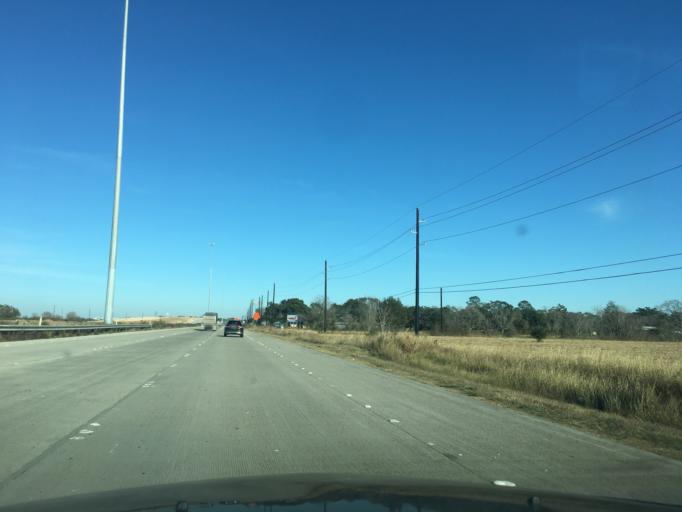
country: US
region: Texas
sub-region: Fort Bend County
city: Rosenberg
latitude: 29.5288
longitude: -95.8655
